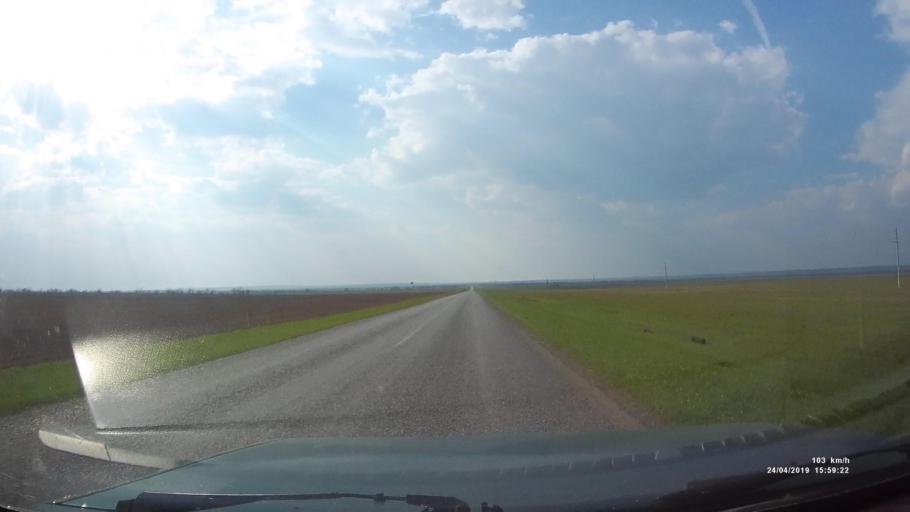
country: RU
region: Rostov
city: Sovetskoye
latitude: 46.6227
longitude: 42.4735
